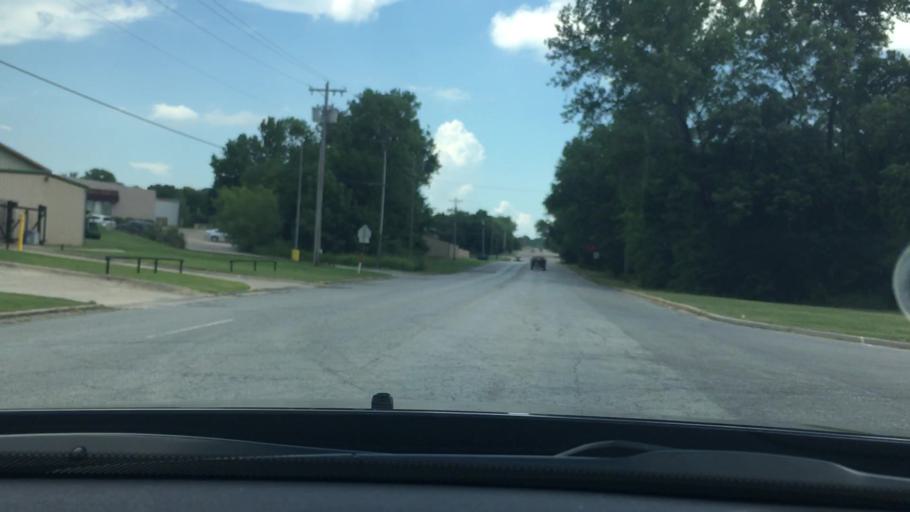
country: US
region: Oklahoma
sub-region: Pontotoc County
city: Ada
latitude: 34.7605
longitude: -96.6612
